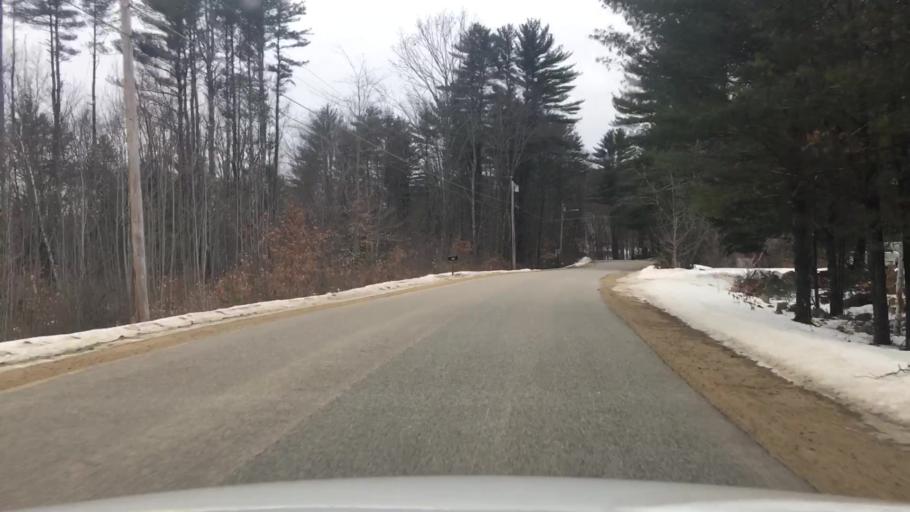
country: US
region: New Hampshire
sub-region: Strafford County
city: Rochester
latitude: 43.3644
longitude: -70.9716
